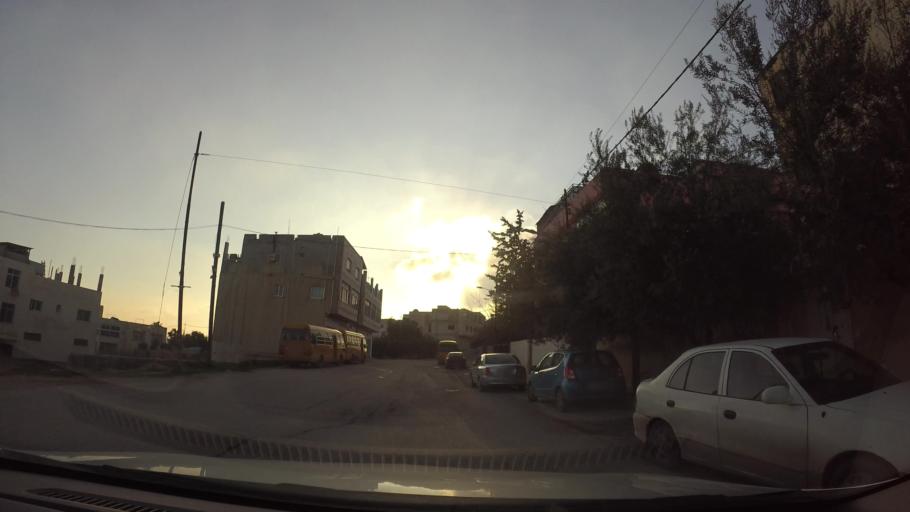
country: JO
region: Amman
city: Al Bunayyat ash Shamaliyah
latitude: 31.9051
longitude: 35.9077
